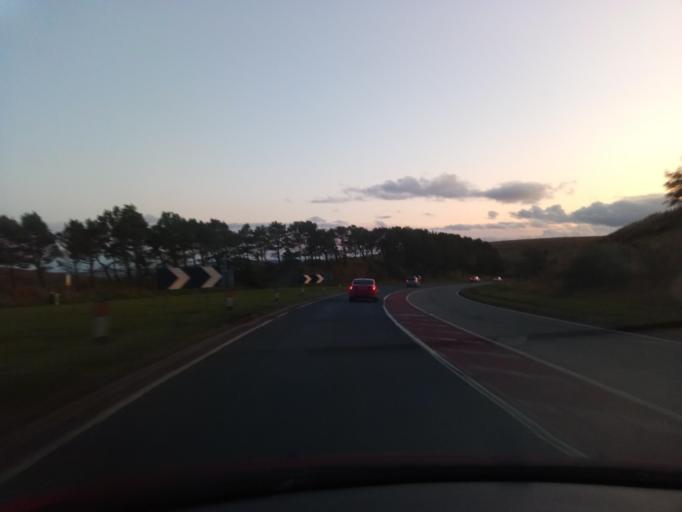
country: GB
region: Scotland
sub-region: East Lothian
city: Pencaitland
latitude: 55.8045
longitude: -2.8349
